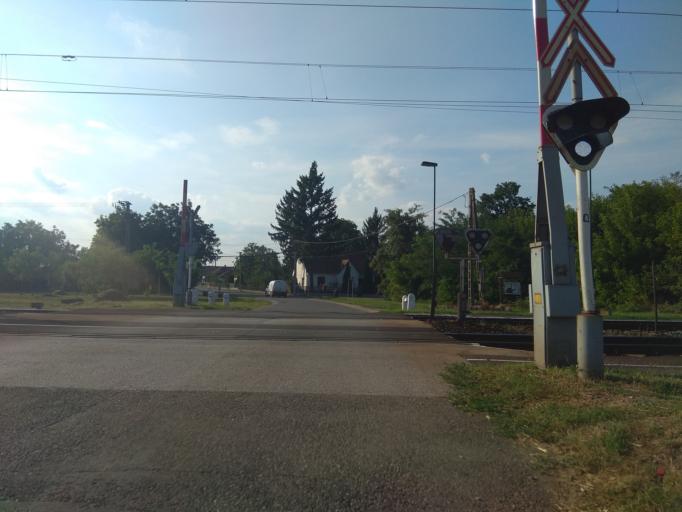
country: HU
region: Borsod-Abauj-Zemplen
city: Emod
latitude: 47.8906
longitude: 20.7637
